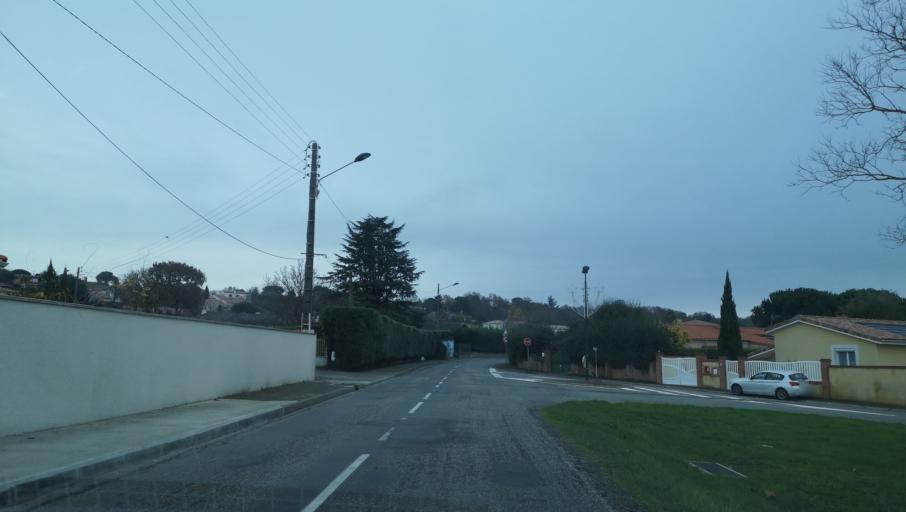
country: FR
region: Midi-Pyrenees
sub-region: Departement de la Haute-Garonne
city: Gratentour
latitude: 43.7228
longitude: 1.4201
